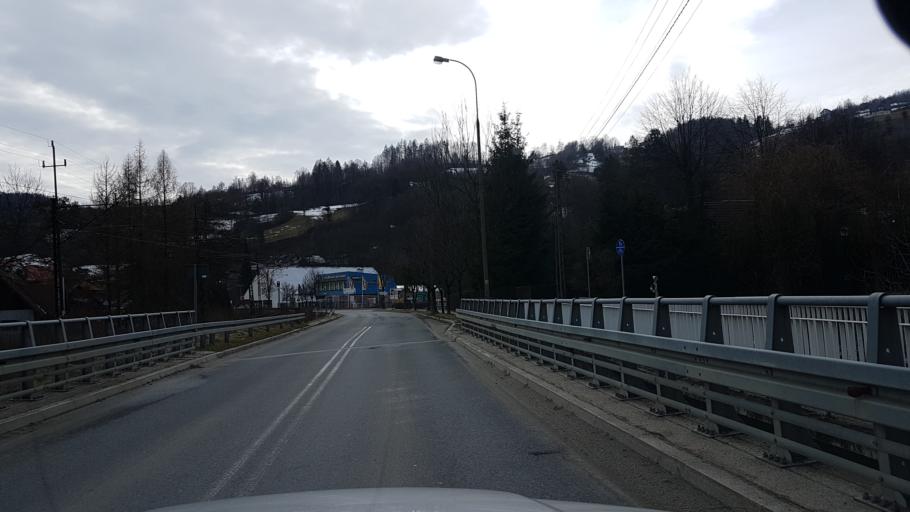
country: PL
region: Lesser Poland Voivodeship
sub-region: Powiat nowosadecki
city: Piwniczna-Zdroj
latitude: 49.4347
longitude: 20.7065
